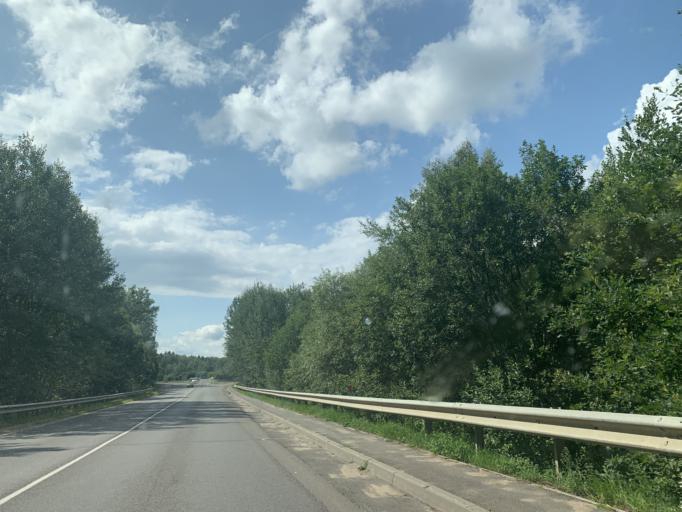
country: BY
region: Minsk
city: Enyerhyetykaw
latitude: 53.5893
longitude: 27.0458
